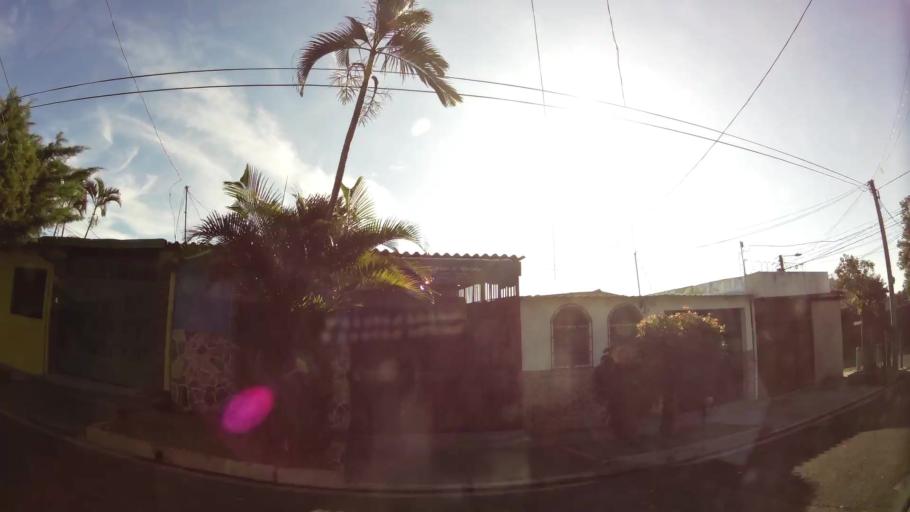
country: SV
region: La Libertad
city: Santa Tecla
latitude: 13.6804
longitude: -89.2843
